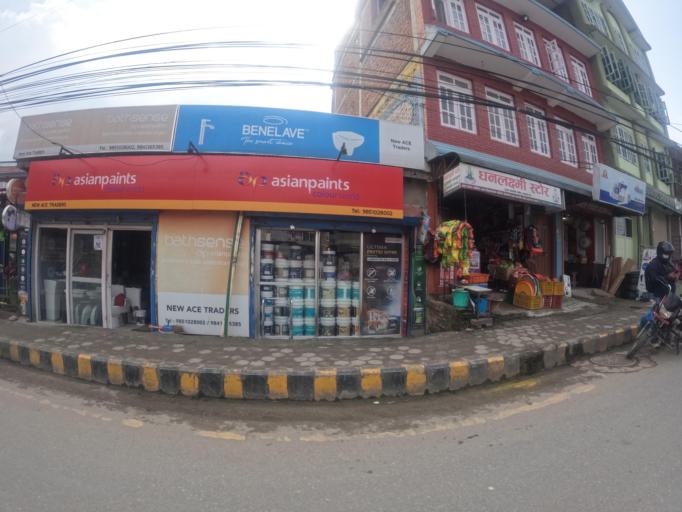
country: NP
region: Central Region
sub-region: Bagmati Zone
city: Bhaktapur
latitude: 27.6693
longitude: 85.3858
